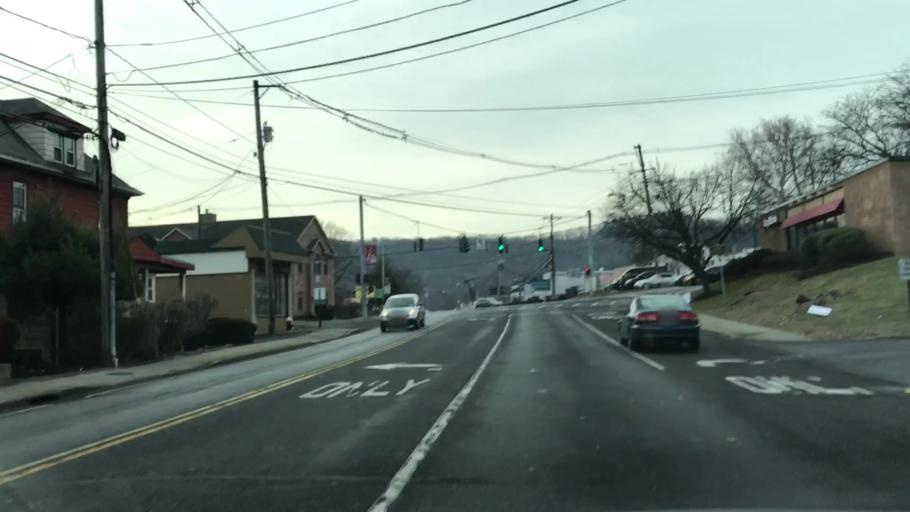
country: US
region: New York
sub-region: Rockland County
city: West Haverstraw
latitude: 41.2104
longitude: -73.9856
